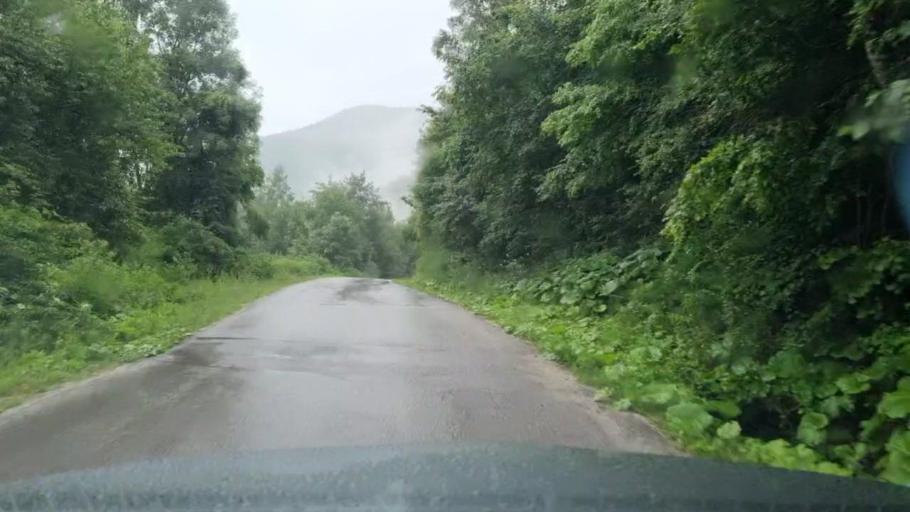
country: BA
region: Federation of Bosnia and Herzegovina
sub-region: Bosansko-Podrinjski Kanton
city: Ustikolina
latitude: 43.6347
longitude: 18.6275
